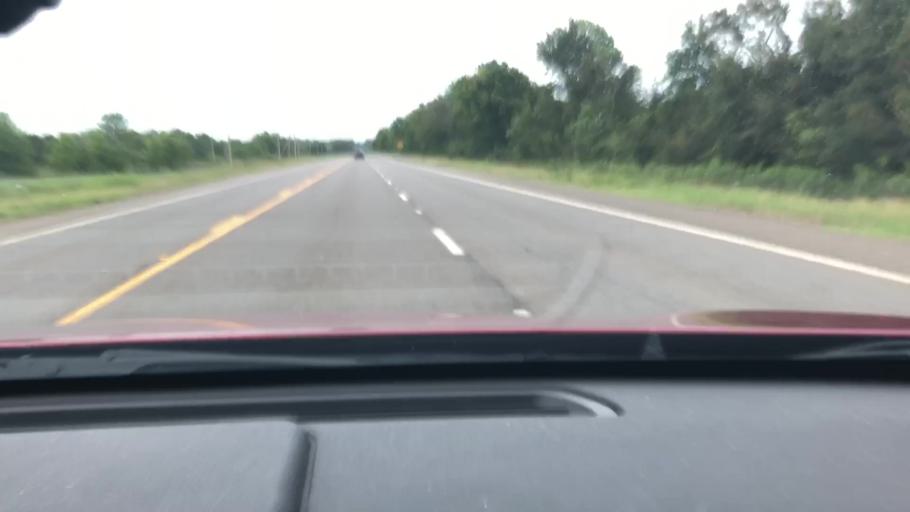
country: US
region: Arkansas
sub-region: Lafayette County
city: Lewisville
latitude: 33.3566
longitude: -93.6477
